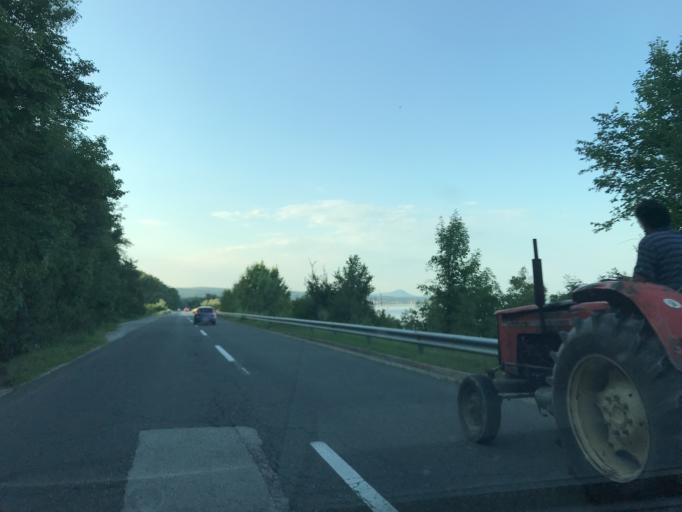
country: RO
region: Mehedinti
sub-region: Comuna Gogosu
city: Ostrovu Mare
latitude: 44.4601
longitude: 22.4515
